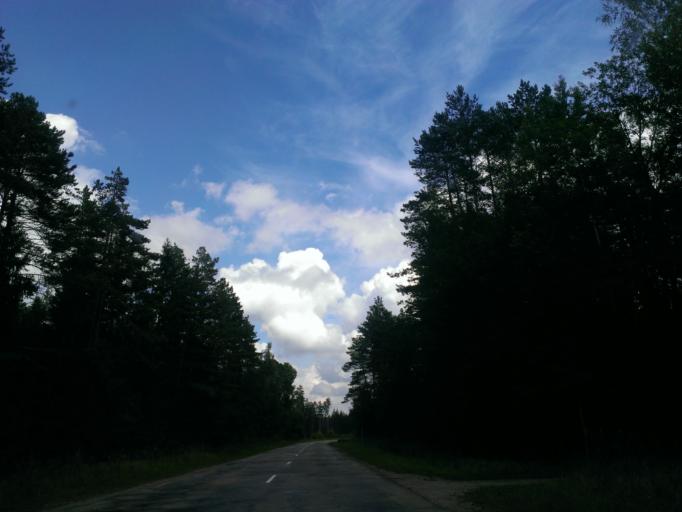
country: LV
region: Ropazu
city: Ropazi
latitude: 57.0238
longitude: 24.6288
